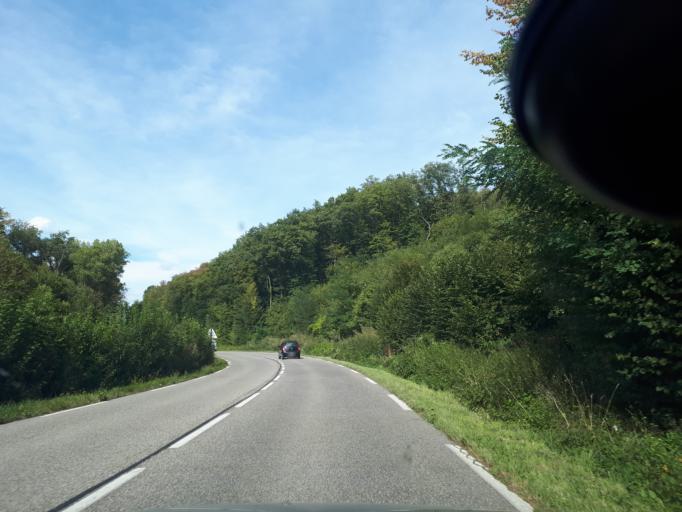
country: FR
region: Rhone-Alpes
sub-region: Departement de l'Isere
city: Chatonnay
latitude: 45.5245
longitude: 5.2166
